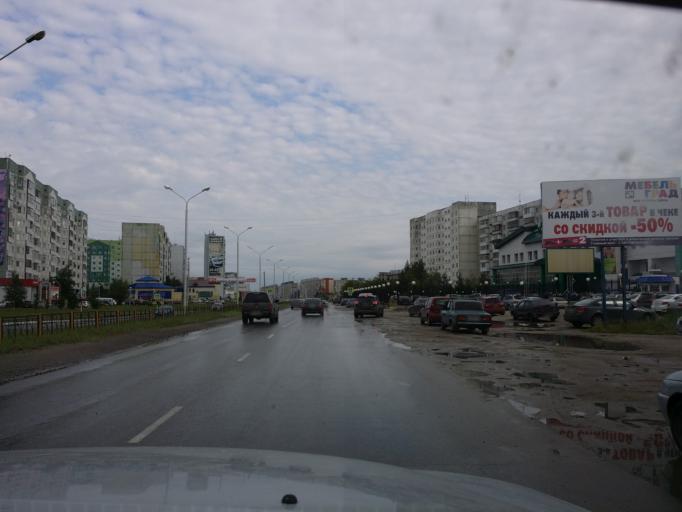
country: RU
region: Khanty-Mansiyskiy Avtonomnyy Okrug
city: Nizhnevartovsk
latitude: 60.9489
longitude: 76.5905
